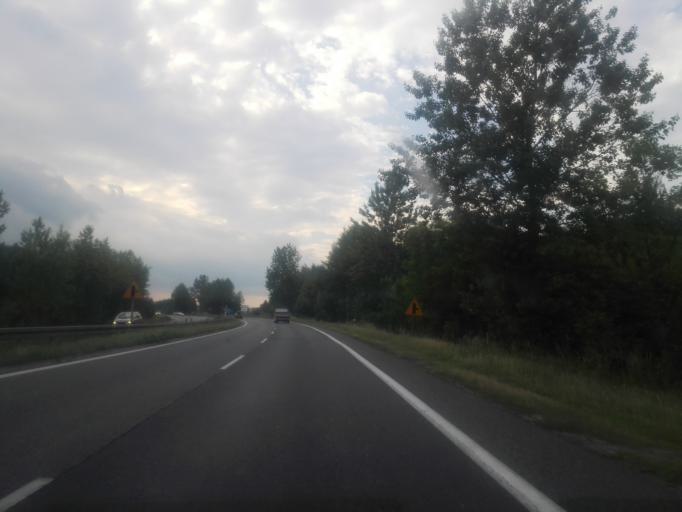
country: PL
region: Silesian Voivodeship
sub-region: Powiat bedzinski
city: Siewierz
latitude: 50.4864
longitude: 19.2170
